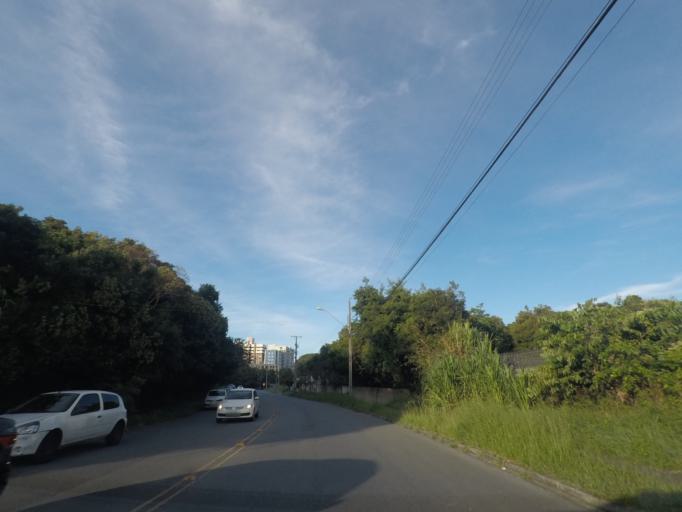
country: BR
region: Parana
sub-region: Curitiba
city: Curitiba
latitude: -25.4025
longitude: -49.2576
